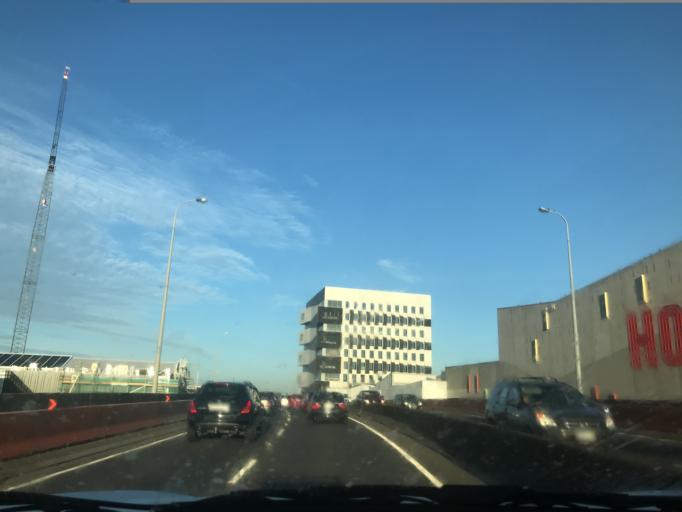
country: NZ
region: Auckland
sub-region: Auckland
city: Tamaki
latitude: -36.9152
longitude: 174.8429
